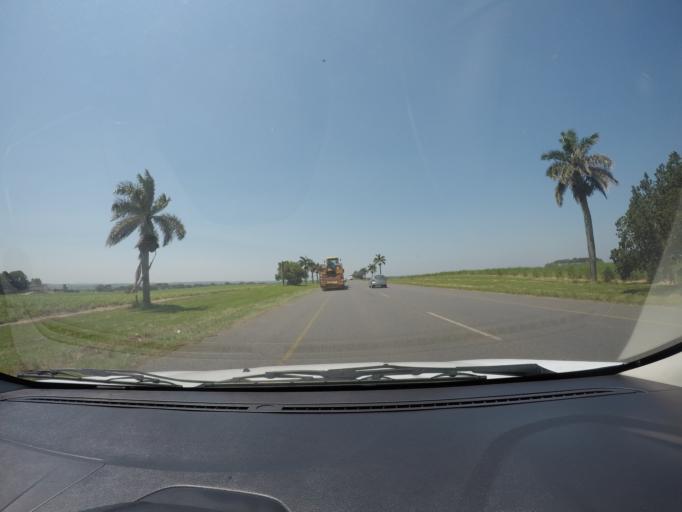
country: ZA
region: KwaZulu-Natal
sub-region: uThungulu District Municipality
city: Empangeni
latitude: -28.8116
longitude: 31.9558
